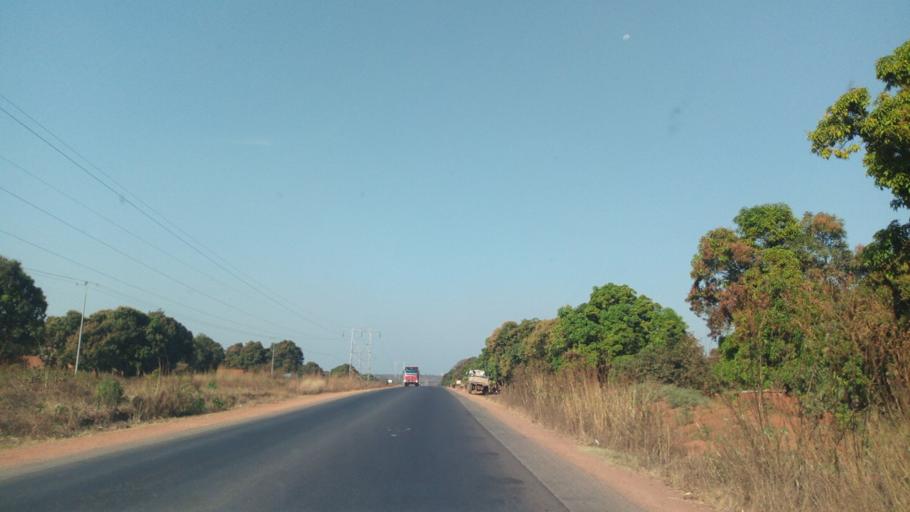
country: CD
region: Katanga
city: Likasi
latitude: -11.0010
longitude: 26.8760
